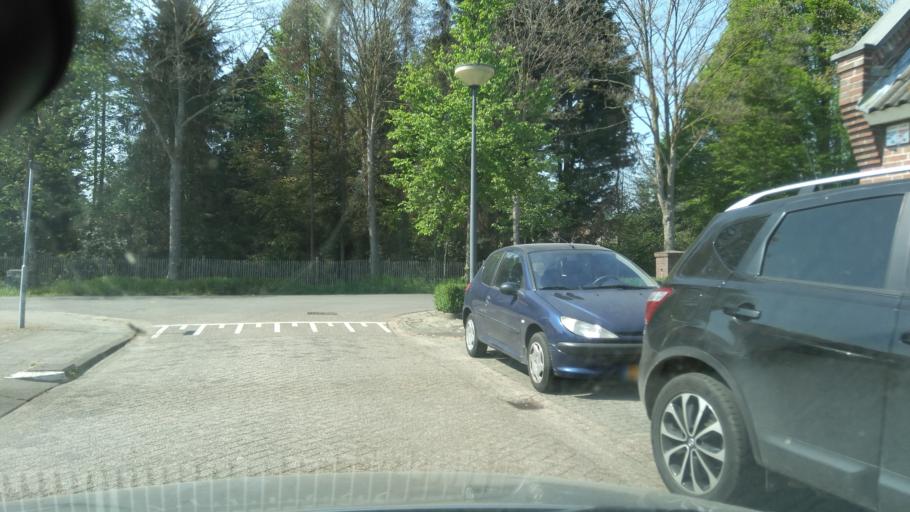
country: BE
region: Flanders
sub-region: Provincie Antwerpen
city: Baarle-Hertog
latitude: 51.4589
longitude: 4.8572
